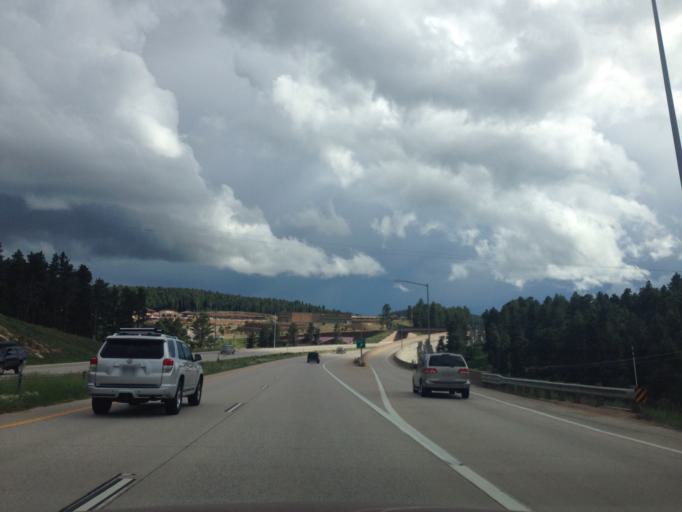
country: US
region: Colorado
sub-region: Jefferson County
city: Evergreen
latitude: 39.5336
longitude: -105.3042
